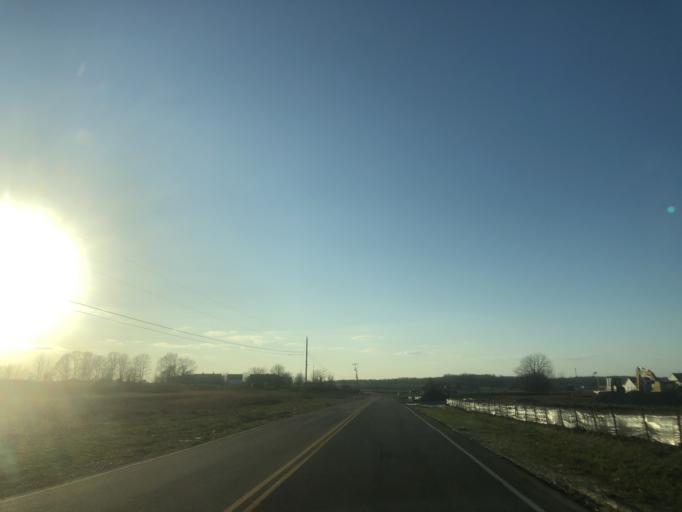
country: US
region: Tennessee
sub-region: Sumner County
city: White House
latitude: 36.4813
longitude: -86.7031
